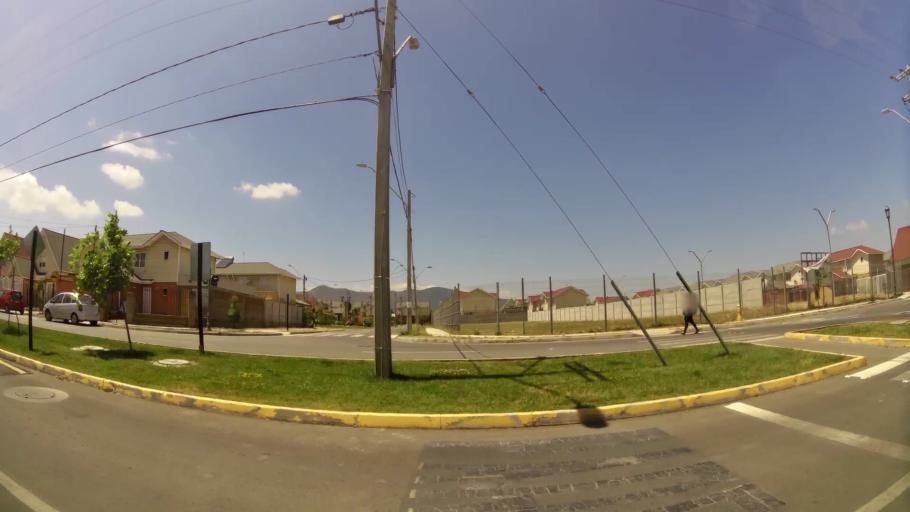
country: CL
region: Santiago Metropolitan
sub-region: Provincia de Talagante
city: Penaflor
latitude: -33.5711
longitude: -70.7943
